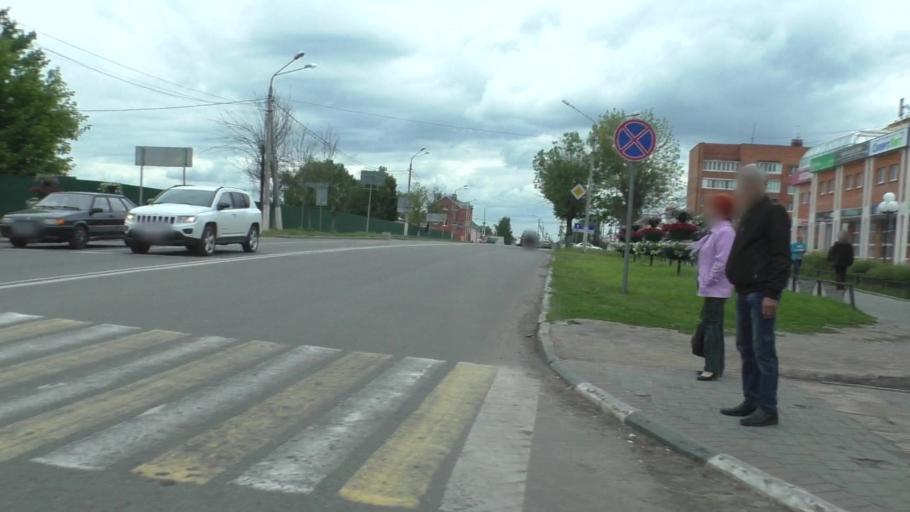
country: RU
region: Moskovskaya
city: Yegor'yevsk
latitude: 55.3779
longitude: 39.0437
